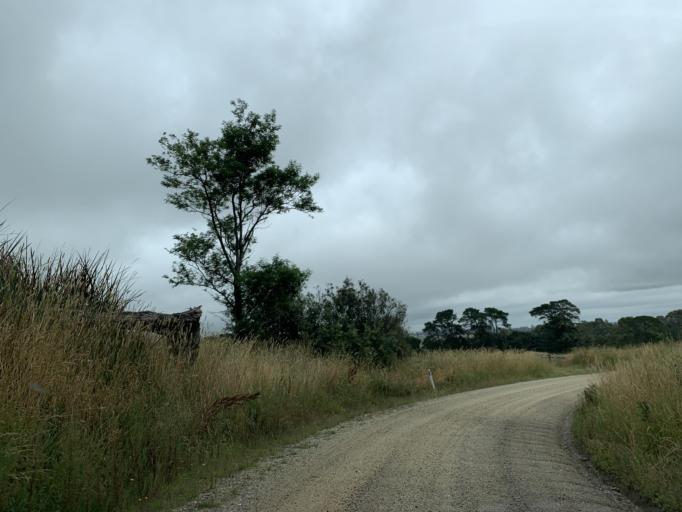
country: AU
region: Victoria
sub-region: Baw Baw
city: Warragul
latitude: -38.3483
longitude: 145.8664
